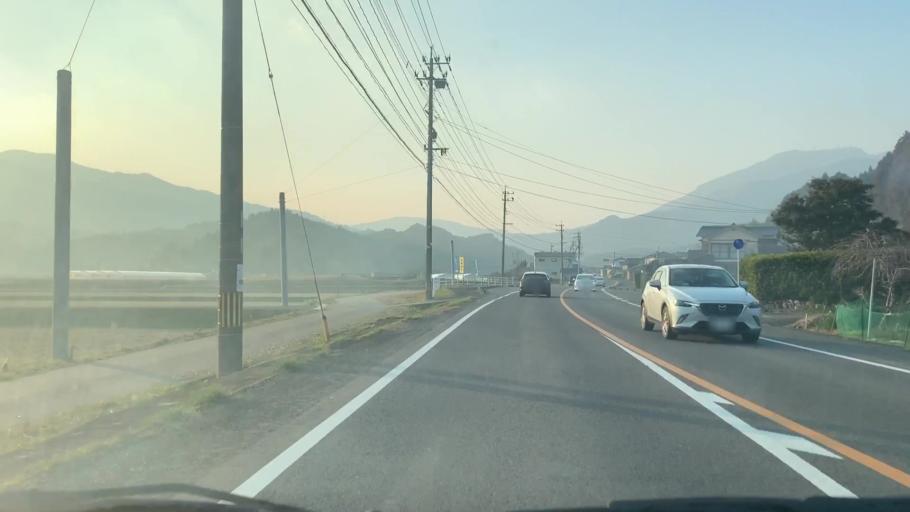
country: JP
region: Saga Prefecture
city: Takeocho-takeo
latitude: 33.2586
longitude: 130.0686
